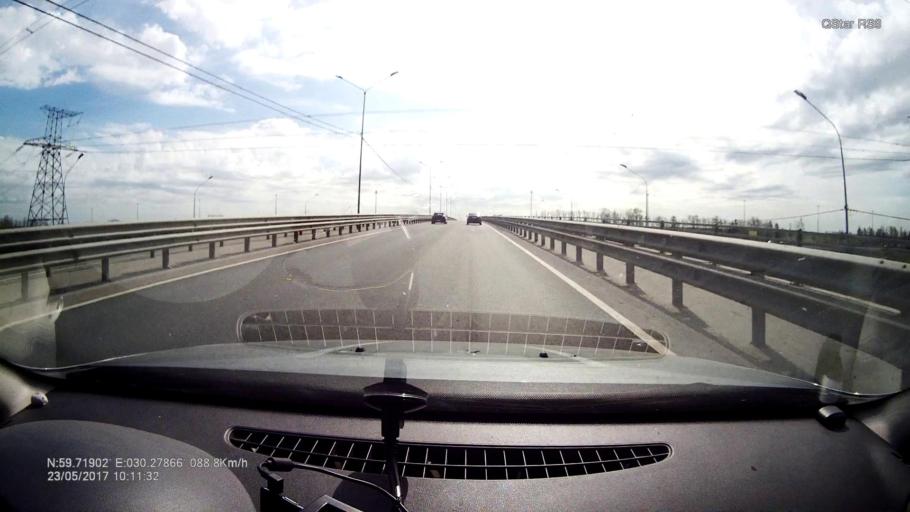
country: RU
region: St.-Petersburg
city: Aleksandrovskaya
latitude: 59.7193
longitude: 30.2777
